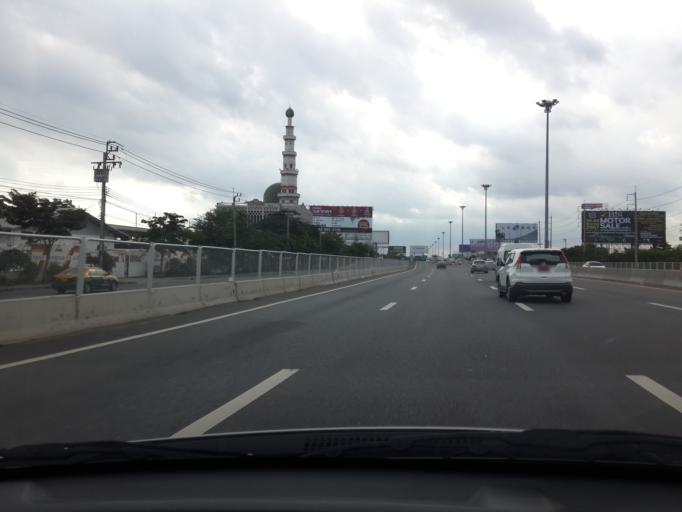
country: TH
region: Bangkok
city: Suan Luang
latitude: 13.7367
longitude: 100.6678
